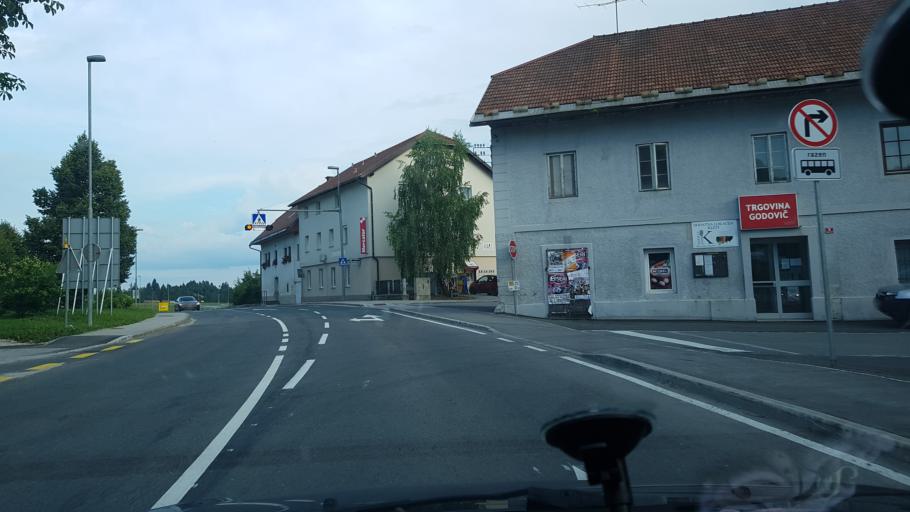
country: SI
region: Idrija
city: Idrija
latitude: 45.9577
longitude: 14.0921
